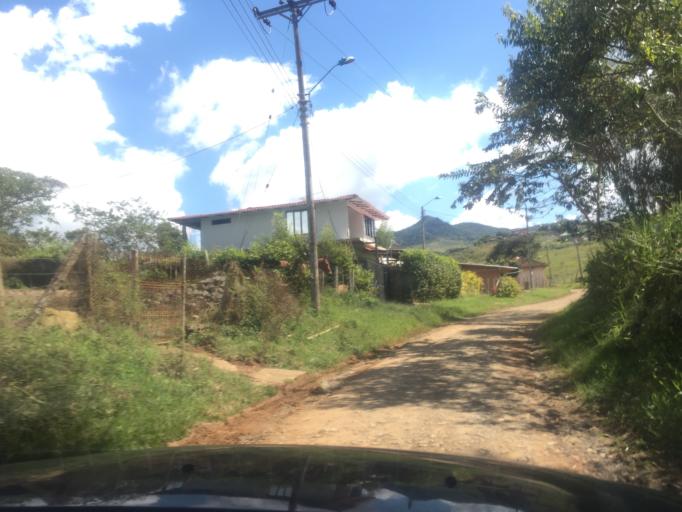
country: CO
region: Valle del Cauca
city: Yumbo
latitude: 3.6632
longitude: -76.5601
